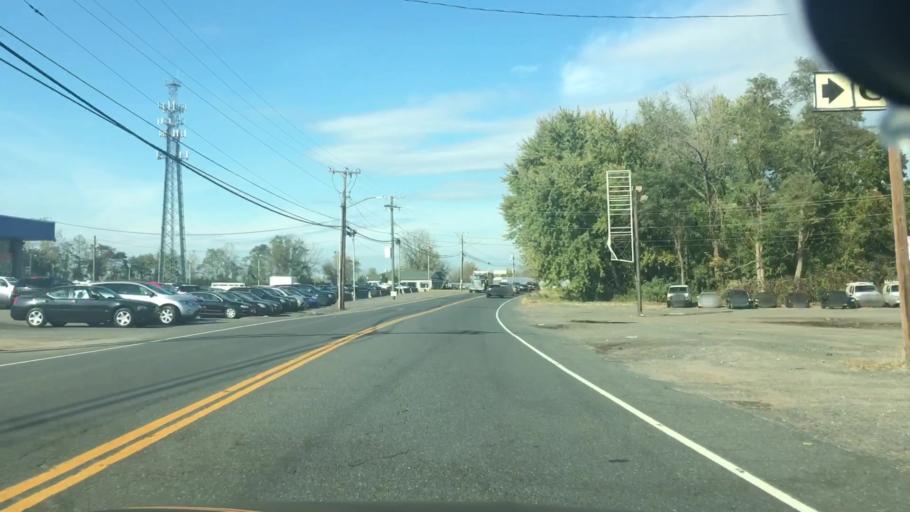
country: US
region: Connecticut
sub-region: Hartford County
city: Windsor
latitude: 41.8752
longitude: -72.6092
